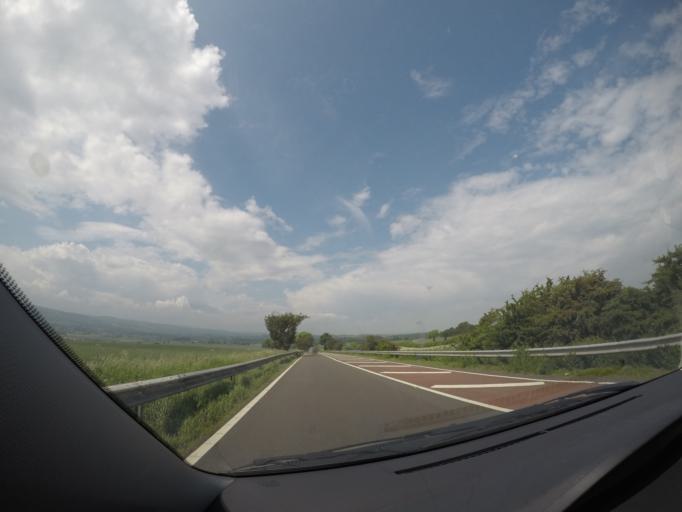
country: GB
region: England
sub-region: County Durham
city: Hutton Magna
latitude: 54.4654
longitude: -1.7396
